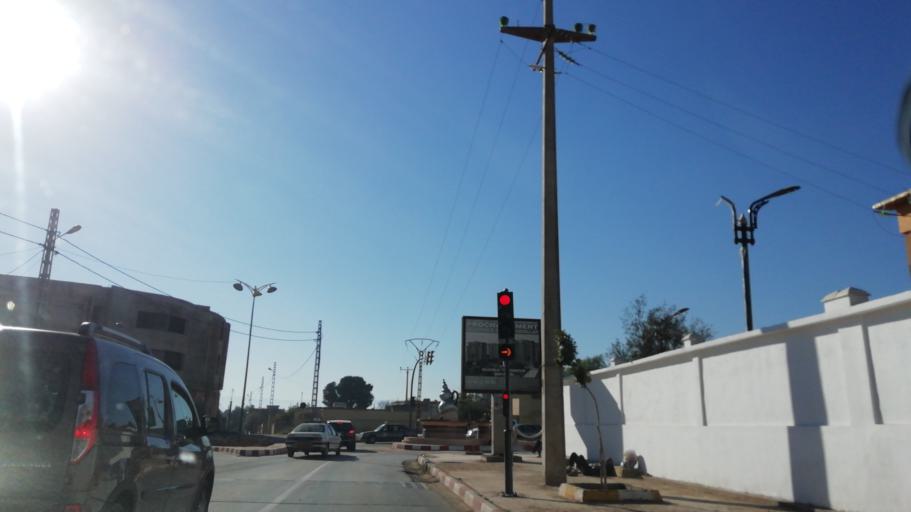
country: DZ
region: Tlemcen
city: Nedroma
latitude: 34.8464
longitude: -1.7396
